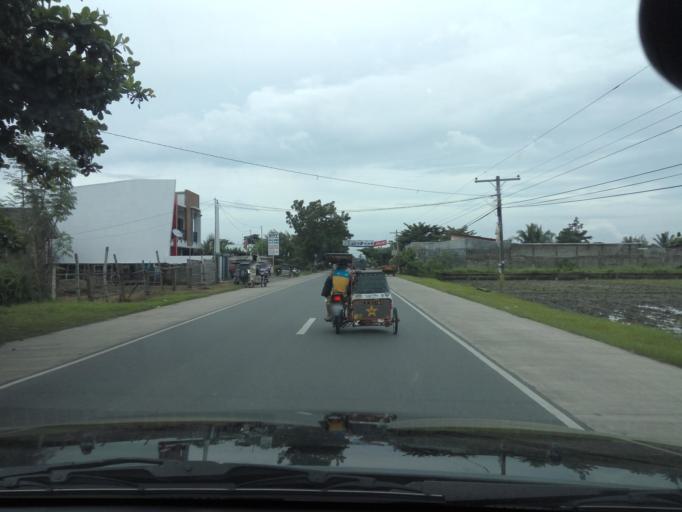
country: PH
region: Central Luzon
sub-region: Province of Nueva Ecija
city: Carmen
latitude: 15.4471
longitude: 120.8175
